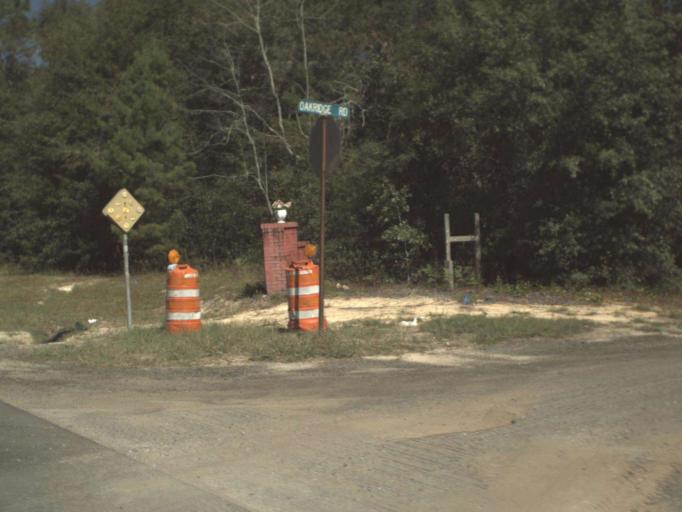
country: US
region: Florida
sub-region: Walton County
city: DeFuniak Springs
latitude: 30.7675
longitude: -86.1549
